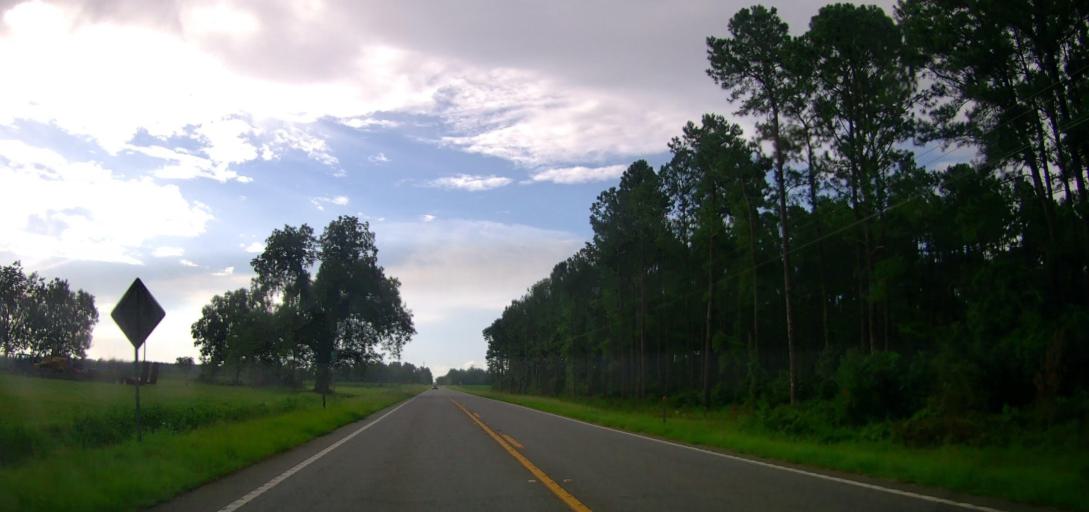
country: US
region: Georgia
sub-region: Ware County
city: Deenwood
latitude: 31.3145
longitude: -82.5703
